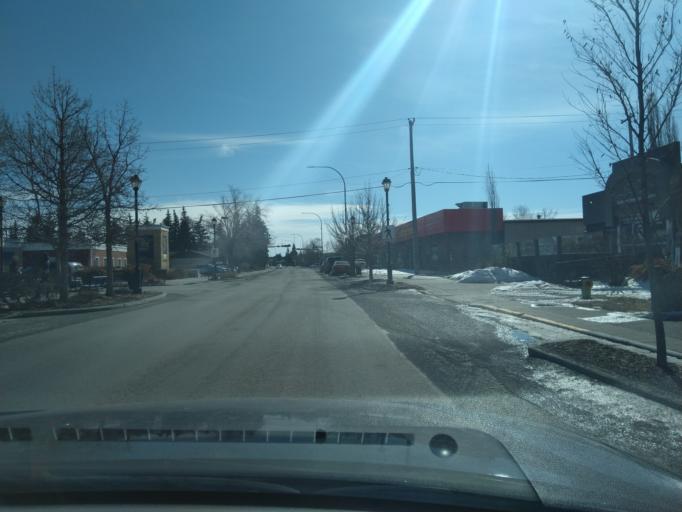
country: CA
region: Alberta
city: Cochrane
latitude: 51.1897
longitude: -114.4690
